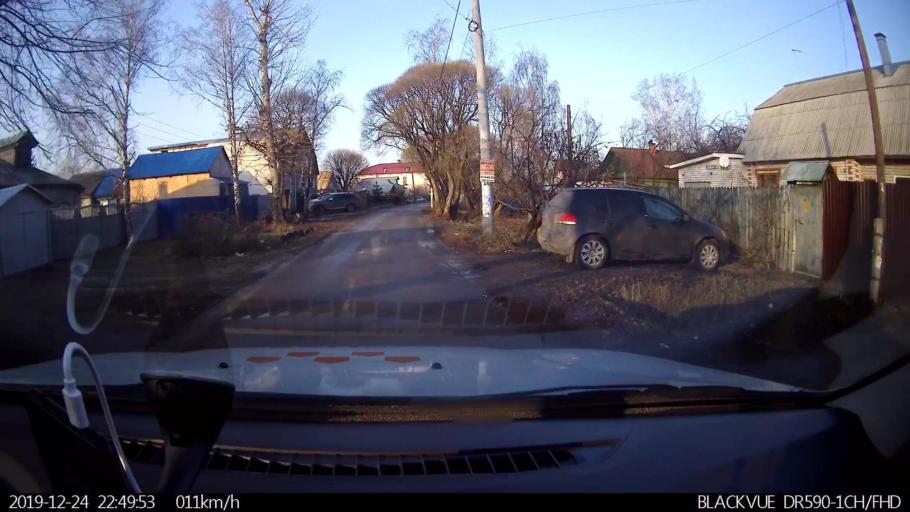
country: RU
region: Nizjnij Novgorod
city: Nizhniy Novgorod
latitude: 56.2881
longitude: 43.8997
